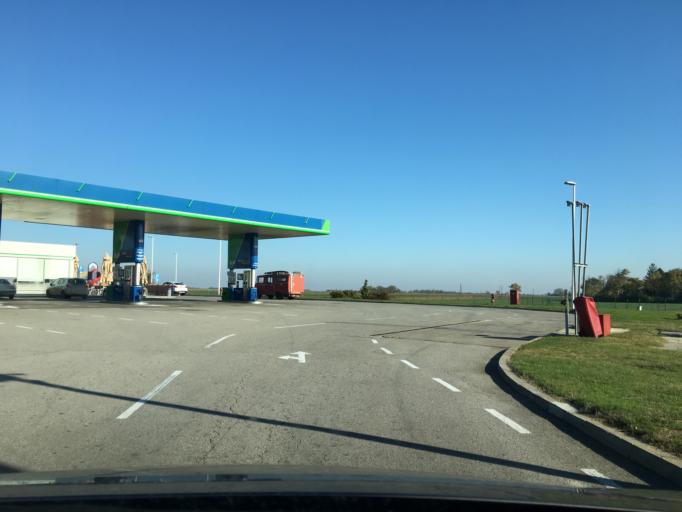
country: RS
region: Autonomna Pokrajina Vojvodina
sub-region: Severnobacki Okrug
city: Backa Topola
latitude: 45.7942
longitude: 19.6941
